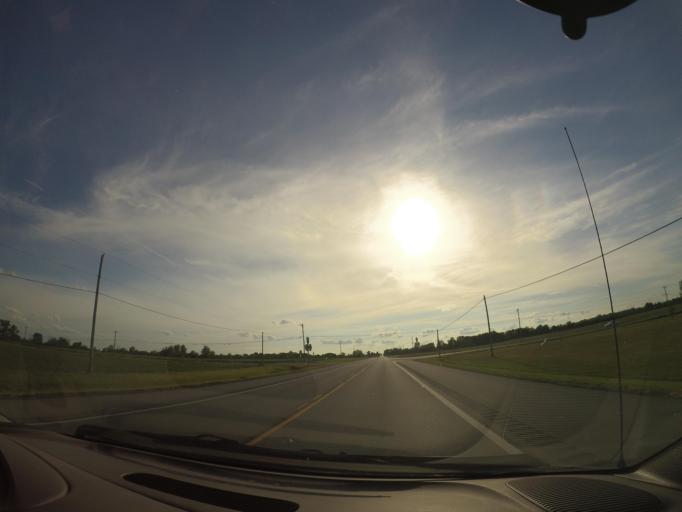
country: US
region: Ohio
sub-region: Williams County
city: Bryan
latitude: 41.4414
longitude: -84.6113
